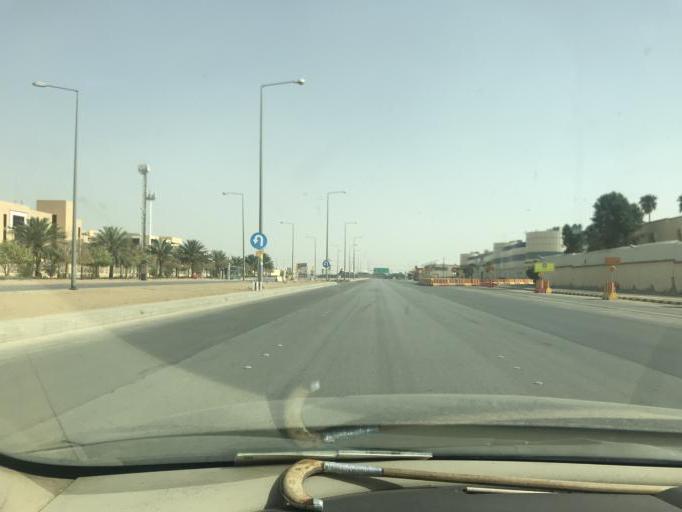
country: SA
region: Ar Riyad
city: Riyadh
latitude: 24.8102
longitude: 46.6916
